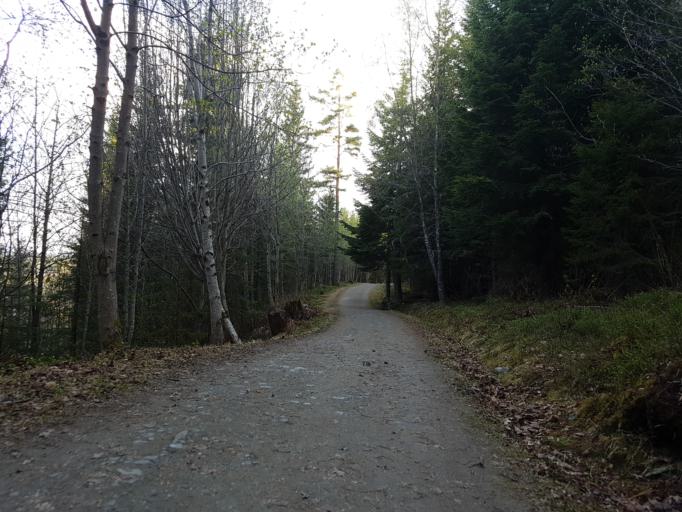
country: NO
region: Sor-Trondelag
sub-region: Trondheim
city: Trondheim
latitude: 63.4316
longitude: 10.3431
